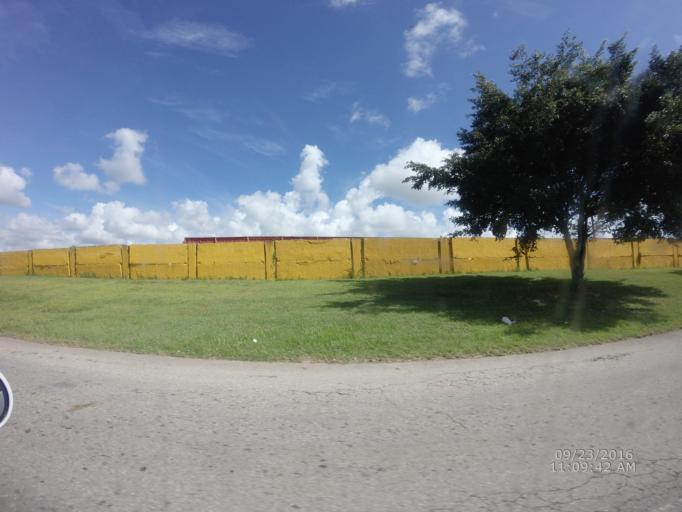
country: CU
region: La Habana
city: Arroyo Naranjo
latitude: 23.0188
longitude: -82.2485
